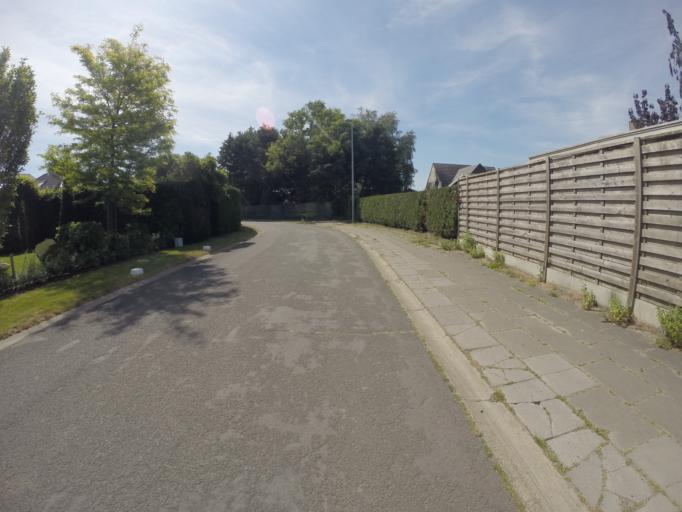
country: BE
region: Flanders
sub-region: Provincie West-Vlaanderen
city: Beernem
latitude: 51.1750
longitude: 3.3340
